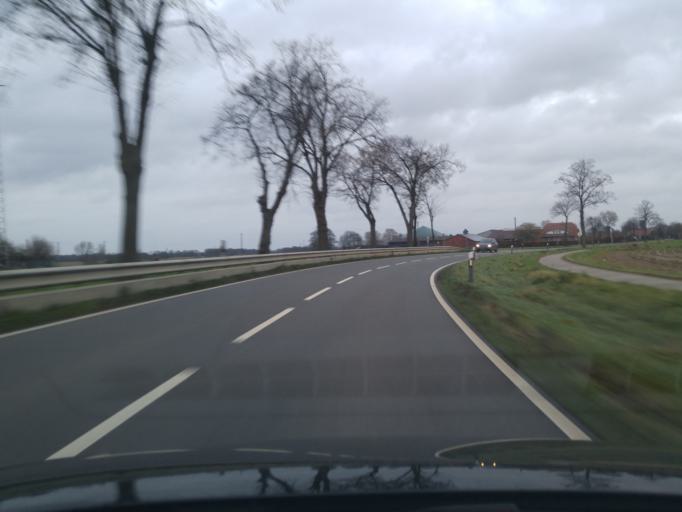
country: DE
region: Lower Saxony
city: Echem
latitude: 53.3380
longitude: 10.5182
